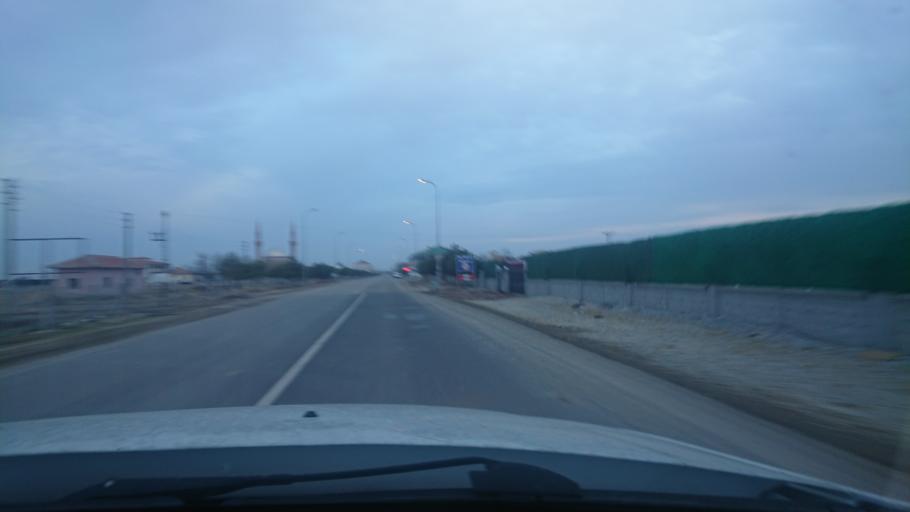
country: TR
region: Aksaray
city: Yesilova
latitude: 38.3310
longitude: 33.7522
